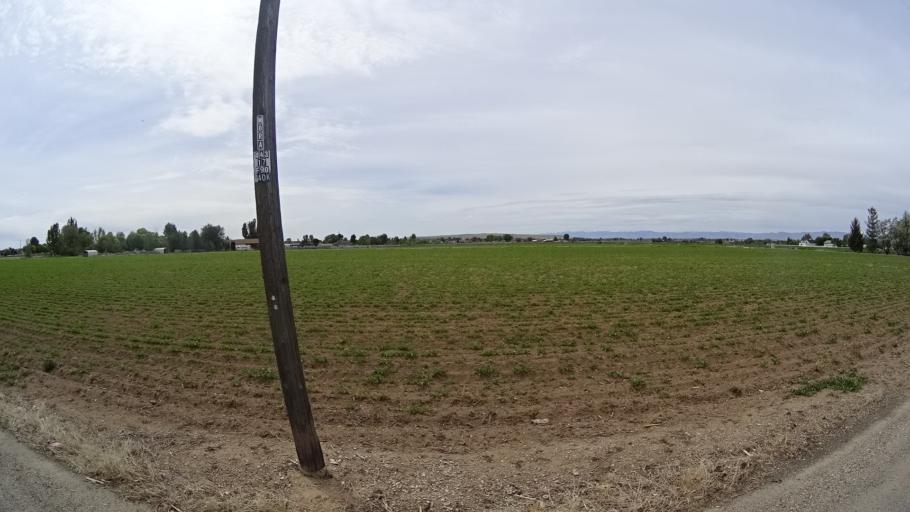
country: US
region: Idaho
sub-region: Ada County
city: Kuna
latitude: 43.5321
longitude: -116.4375
